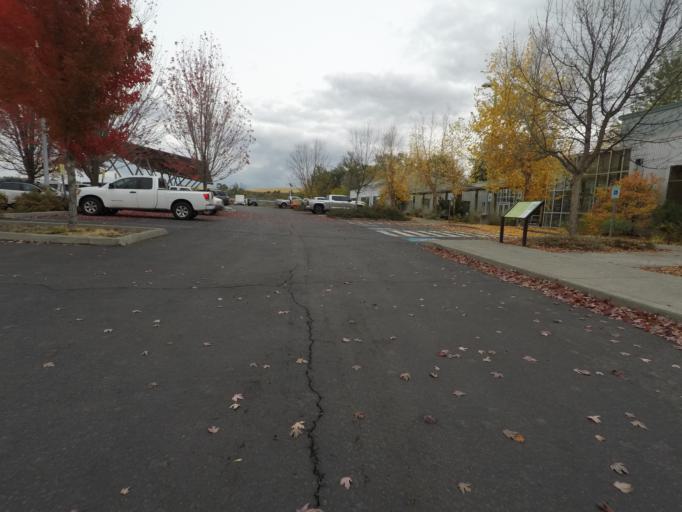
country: US
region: Washington
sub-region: Walla Walla County
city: Walla Walla East
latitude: 46.0781
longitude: -118.2744
